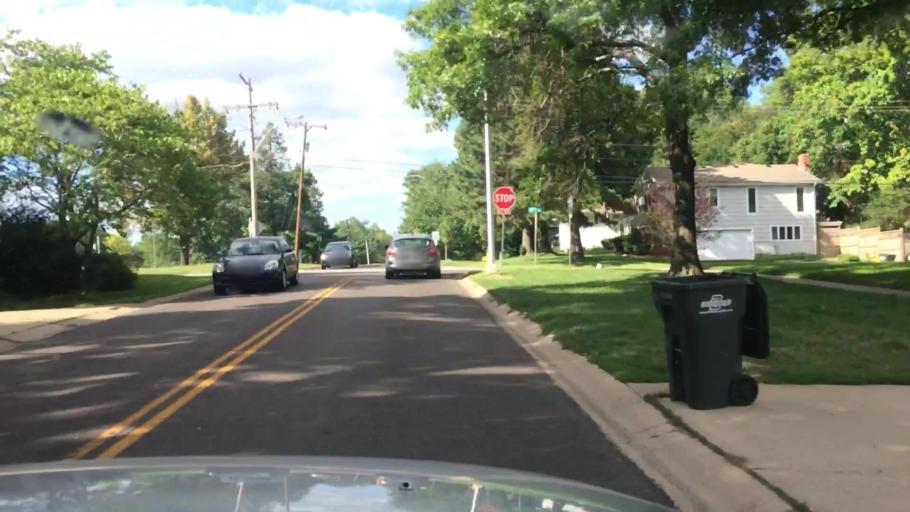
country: US
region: Kansas
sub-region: Johnson County
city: Overland Park
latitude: 38.9709
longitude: -94.6583
